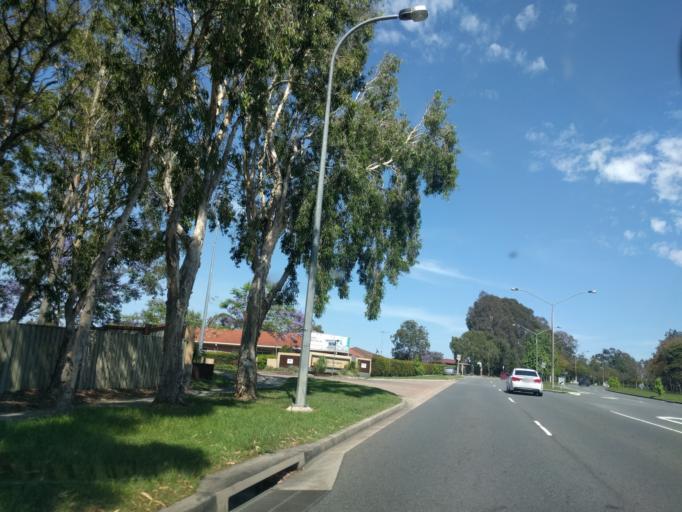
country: AU
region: Queensland
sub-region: Brisbane
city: Richlands
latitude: -27.6094
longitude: 152.9533
